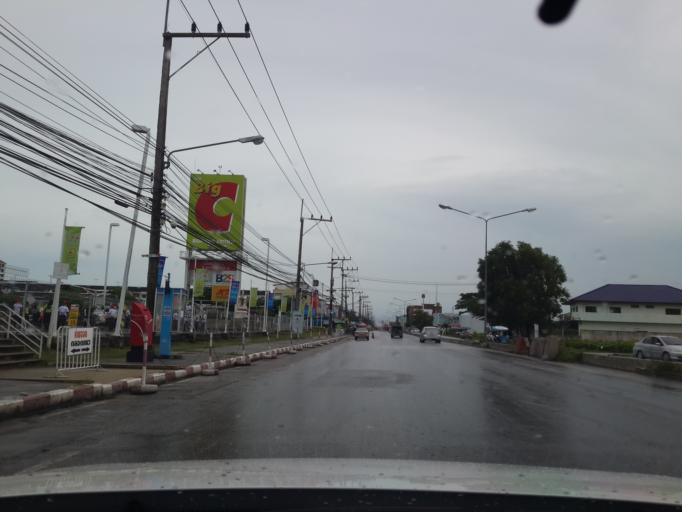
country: TH
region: Pattani
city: Pattani
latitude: 6.8608
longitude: 101.2315
